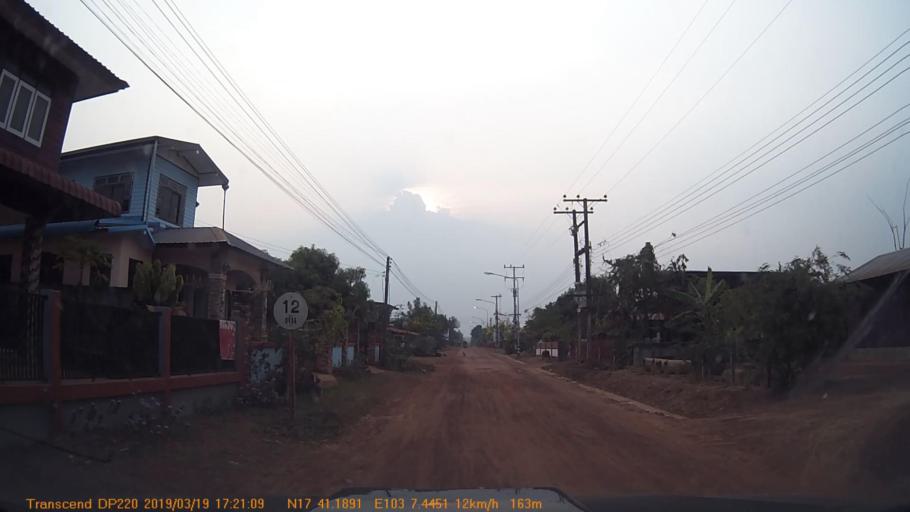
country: TH
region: Changwat Udon Thani
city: Ban Dung
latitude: 17.6865
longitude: 103.1240
